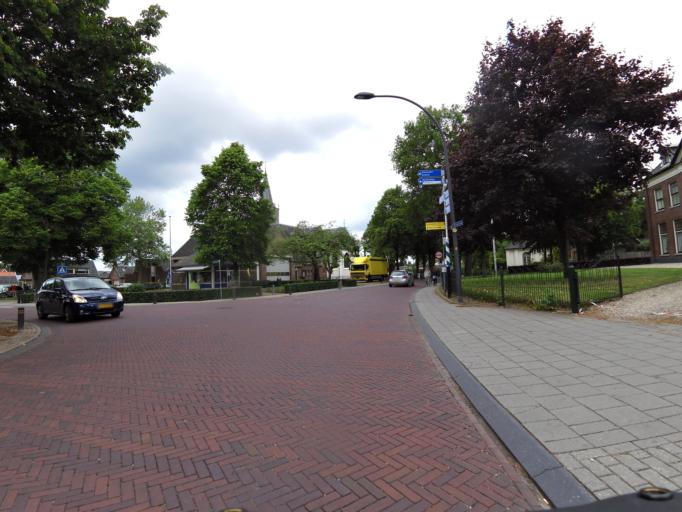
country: NL
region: Gelderland
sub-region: Gemeente Apeldoorn
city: Uddel
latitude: 52.2917
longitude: 5.7879
